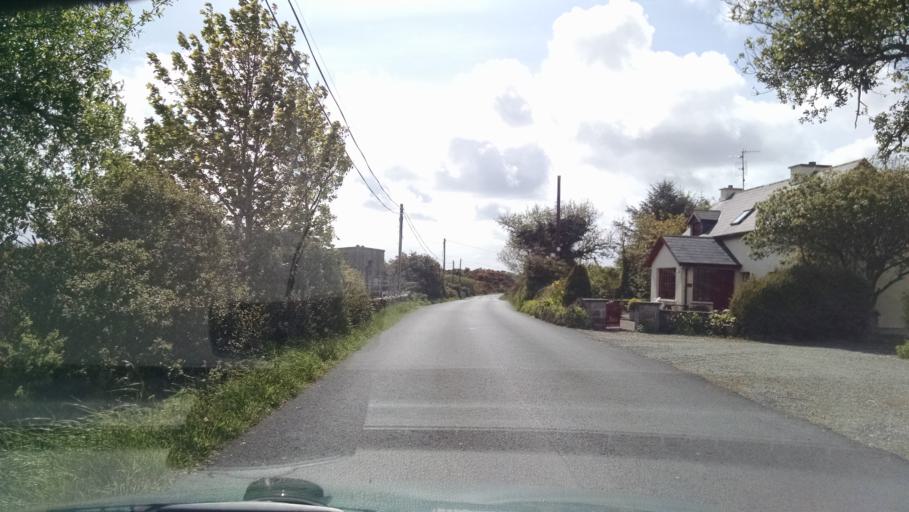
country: IE
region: Connaught
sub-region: County Galway
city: Clifden
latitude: 53.3917
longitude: -9.9264
